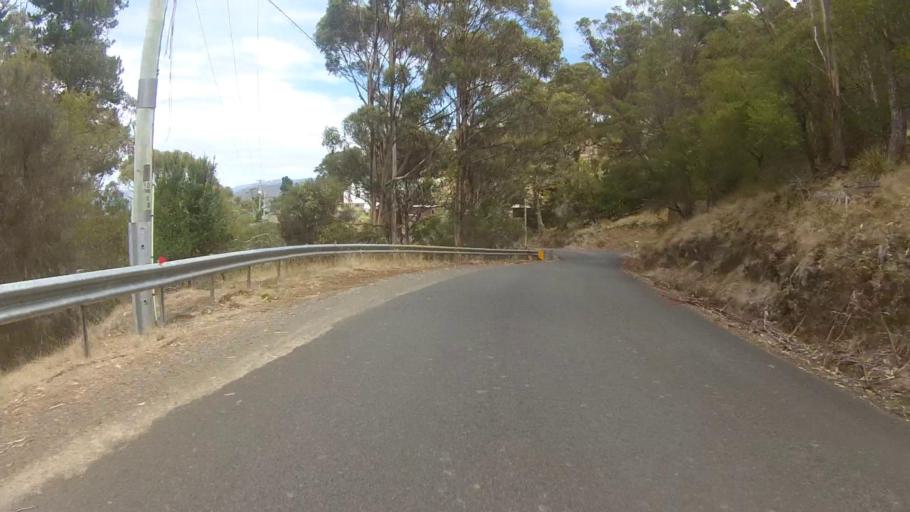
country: AU
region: Tasmania
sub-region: Kingborough
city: Blackmans Bay
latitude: -43.0538
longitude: 147.3375
